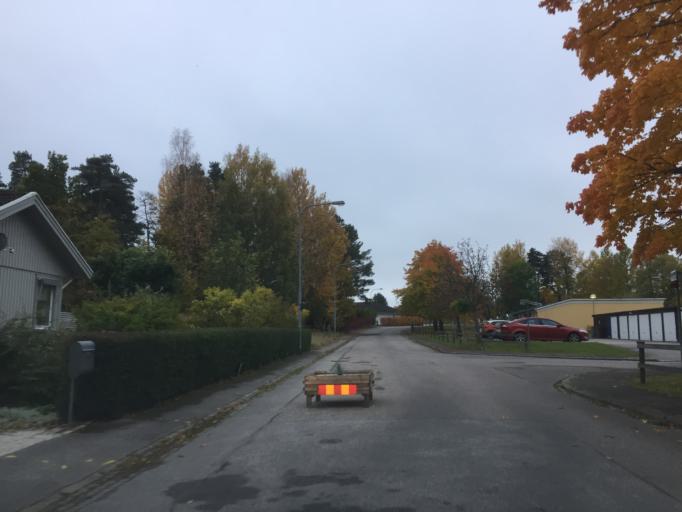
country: SE
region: Vaestra Goetaland
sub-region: Trollhattan
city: Trollhattan
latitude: 58.2920
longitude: 12.3325
